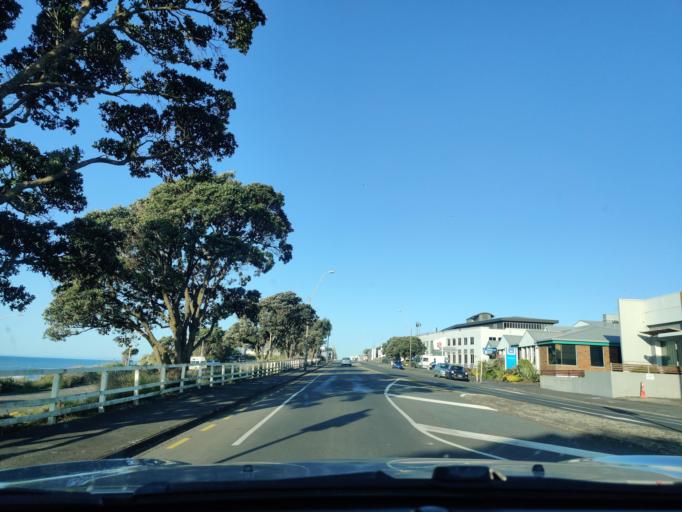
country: NZ
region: Taranaki
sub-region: New Plymouth District
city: New Plymouth
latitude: -39.0554
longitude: 174.0752
